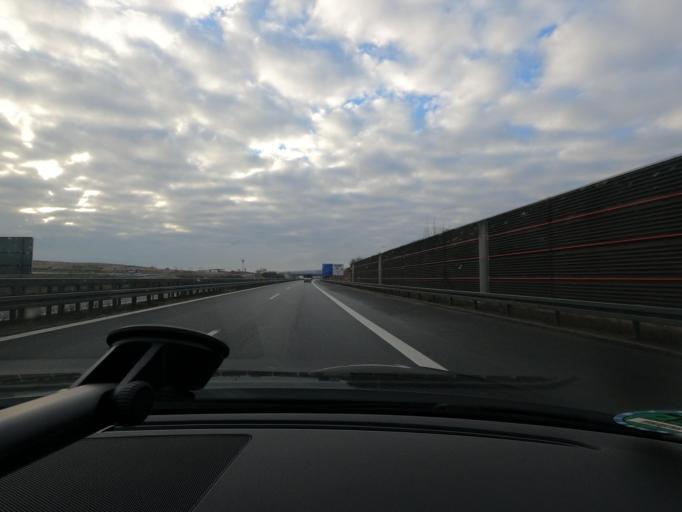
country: DE
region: Bavaria
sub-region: Upper Franconia
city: Rodental
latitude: 50.2280
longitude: 11.0505
